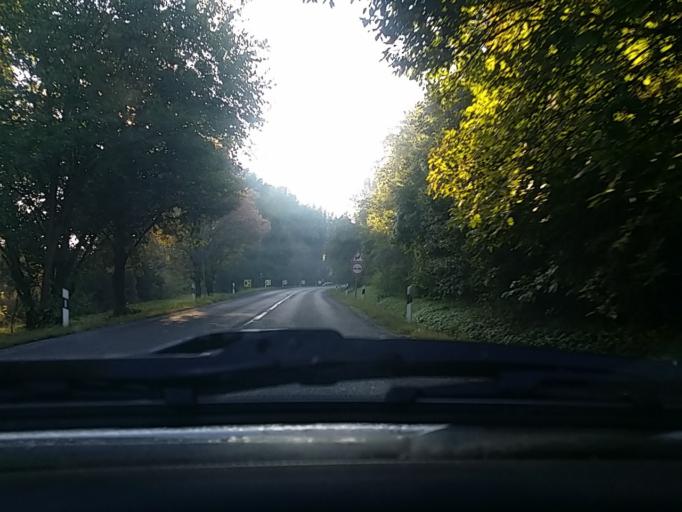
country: HU
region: Pest
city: Szob
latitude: 47.8003
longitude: 18.8562
